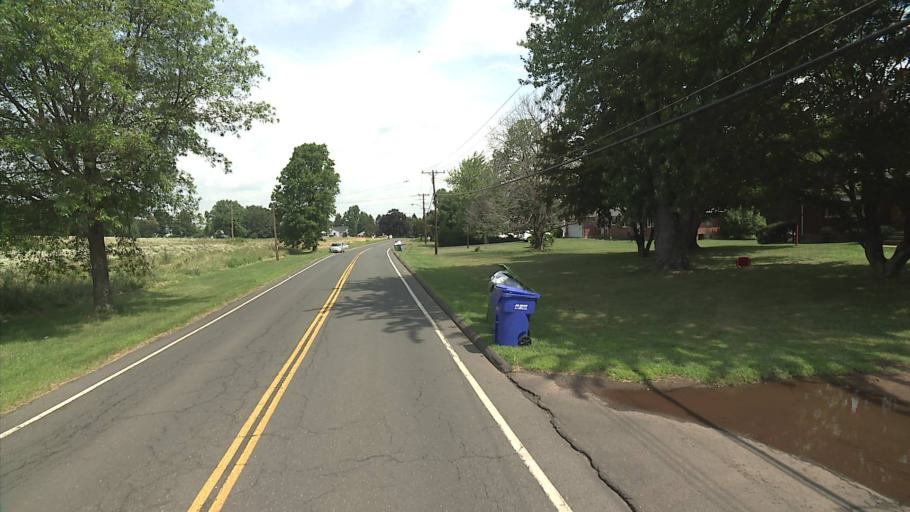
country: US
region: Connecticut
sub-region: Middlesex County
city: Middletown
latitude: 41.5688
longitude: -72.7025
